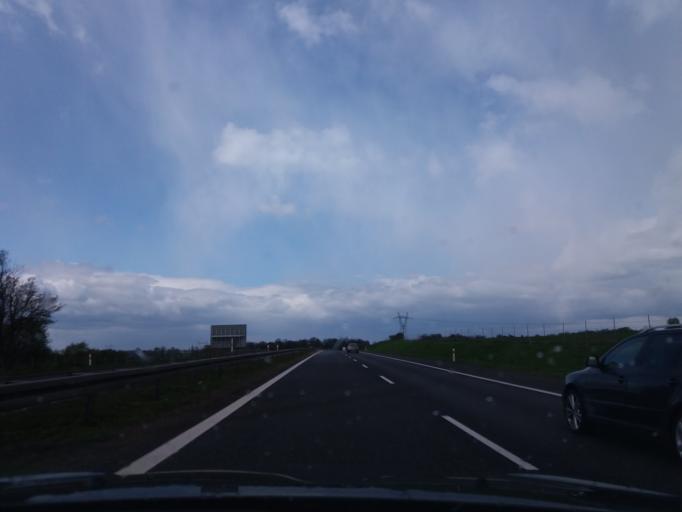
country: PL
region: Silesian Voivodeship
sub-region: Powiat gliwicki
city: Rudziniec
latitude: 50.4006
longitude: 18.4281
